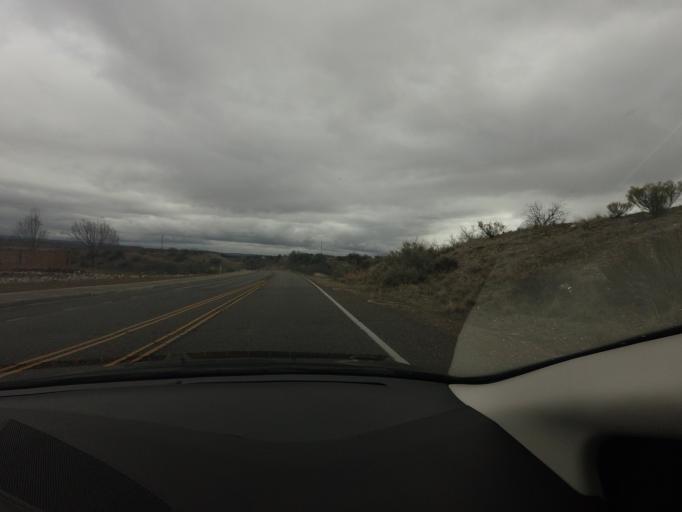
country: US
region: Arizona
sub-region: Yavapai County
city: Cottonwood
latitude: 34.7517
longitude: -112.0338
